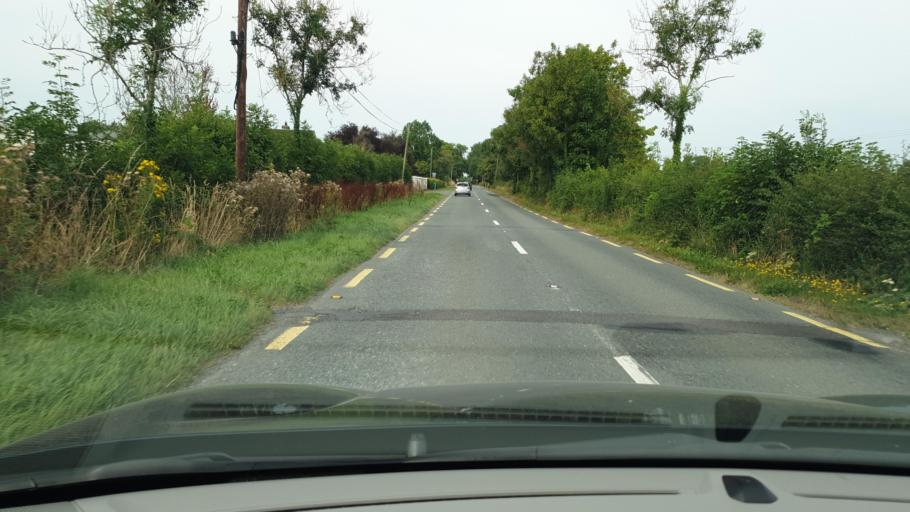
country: IE
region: Leinster
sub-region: An Mhi
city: Athboy
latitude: 53.6440
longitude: -6.8499
